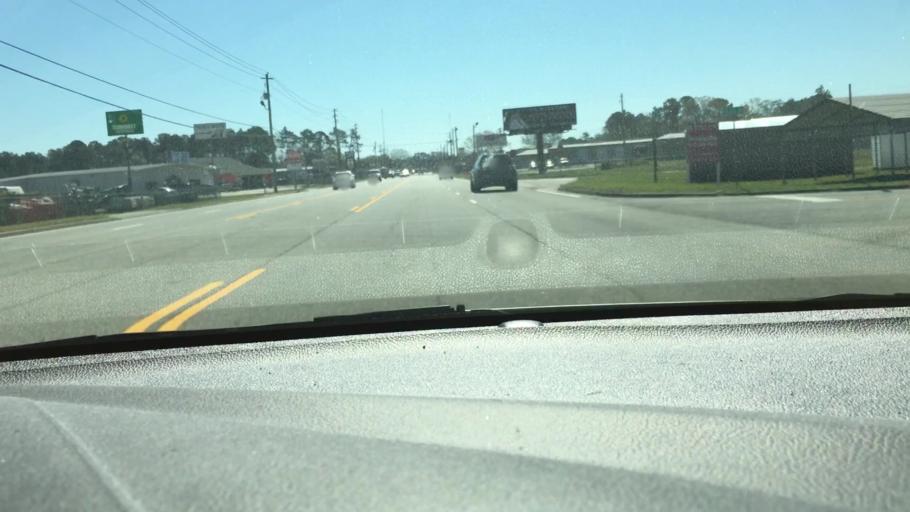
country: US
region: Georgia
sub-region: Glynn County
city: Dock Junction
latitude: 31.2003
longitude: -81.4931
